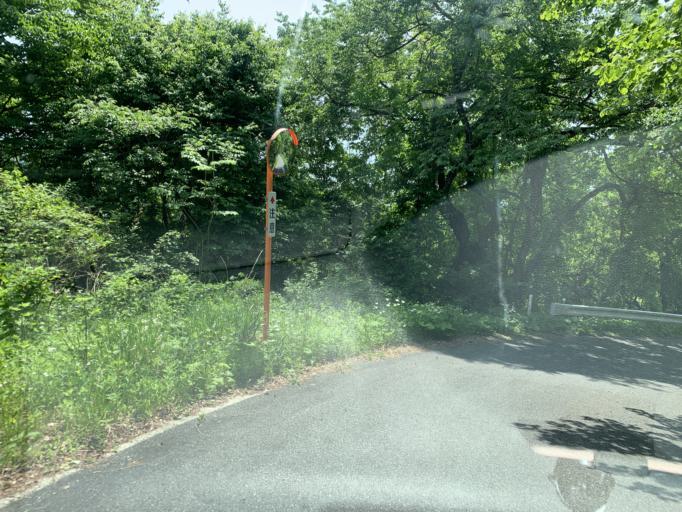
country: JP
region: Iwate
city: Ichinoseki
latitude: 38.9673
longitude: 141.2321
